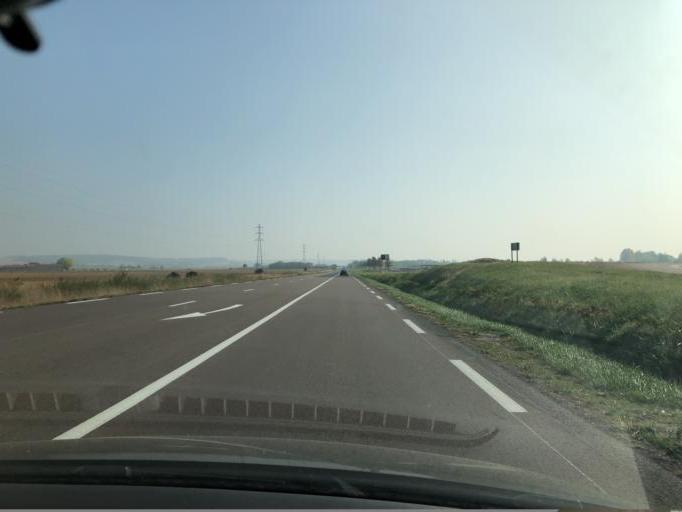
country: FR
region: Bourgogne
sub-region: Departement de l'Yonne
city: Saint-Martin-du-Tertre
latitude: 48.2281
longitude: 3.2763
